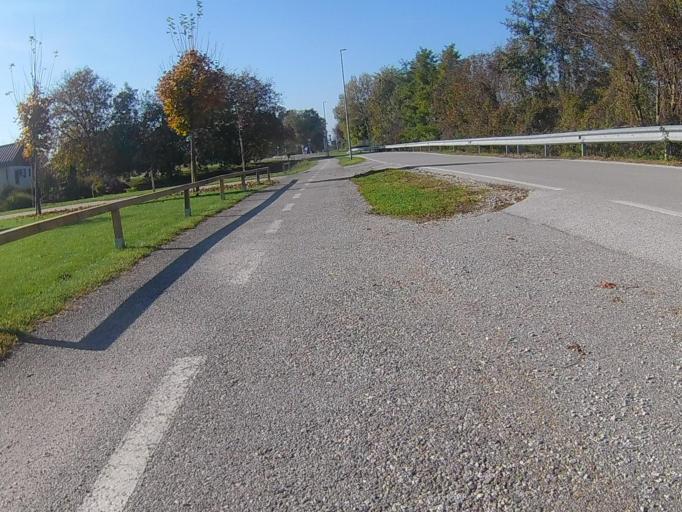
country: SI
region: Hajdina
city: Spodnja Hajdina
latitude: 46.4318
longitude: 15.8322
